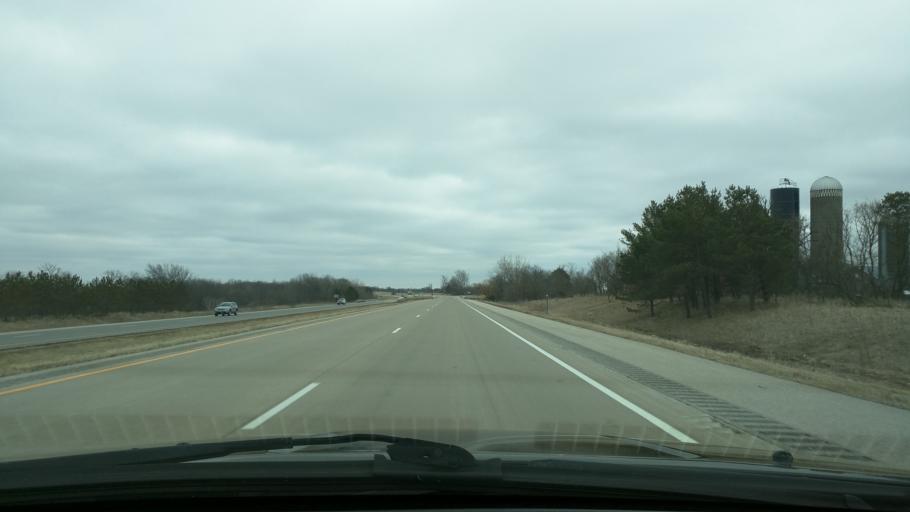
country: US
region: Minnesota
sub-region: Winona County
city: Lewiston
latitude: 43.9343
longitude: -91.9628
